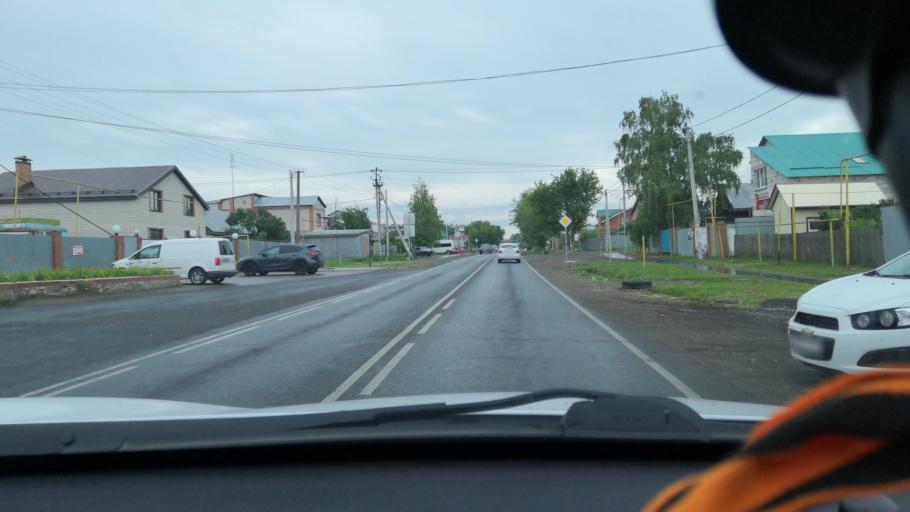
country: RU
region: Samara
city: Novosemeykino
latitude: 53.3753
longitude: 50.3474
